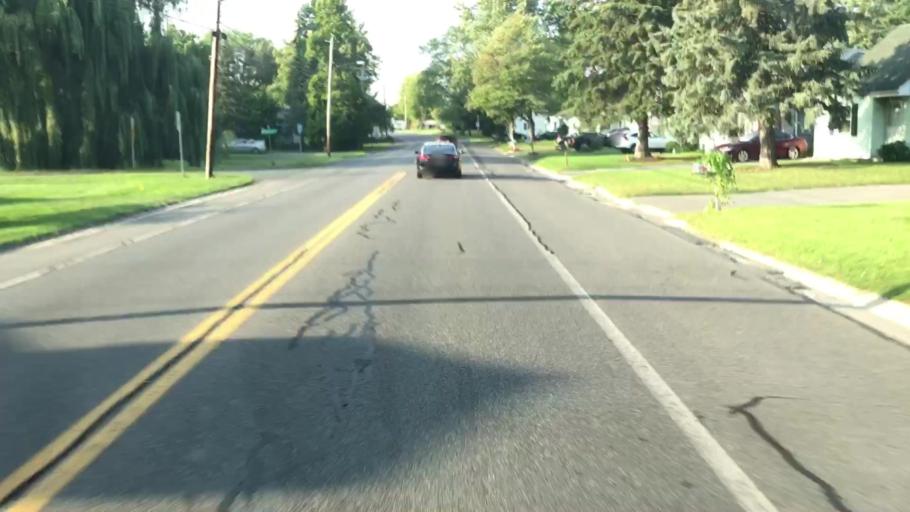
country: US
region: New York
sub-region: Onondaga County
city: Mattydale
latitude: 43.1158
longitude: -76.1593
